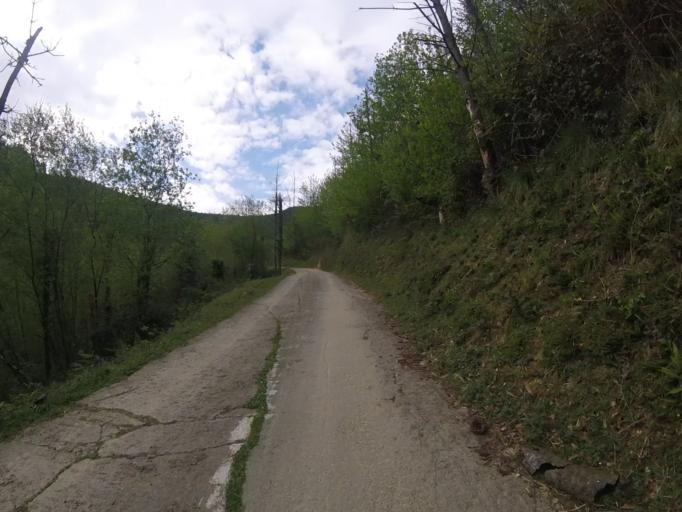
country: ES
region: Basque Country
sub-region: Provincia de Guipuzcoa
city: Errezil
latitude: 43.2027
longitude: -2.1849
